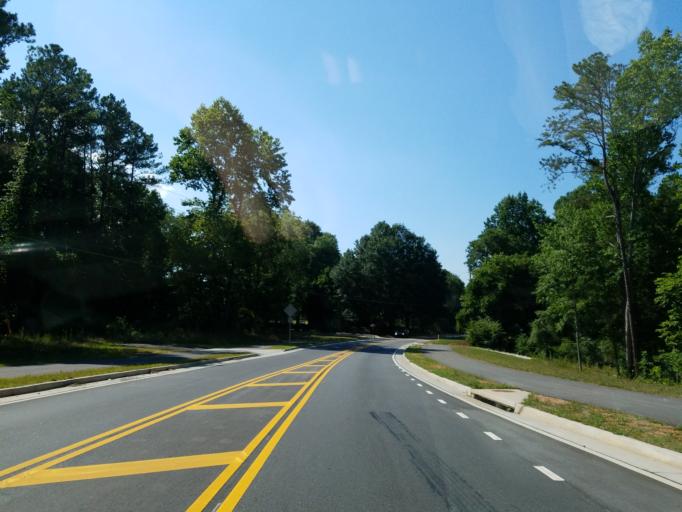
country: US
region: Georgia
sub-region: Fulton County
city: Milton
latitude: 34.1208
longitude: -84.3432
